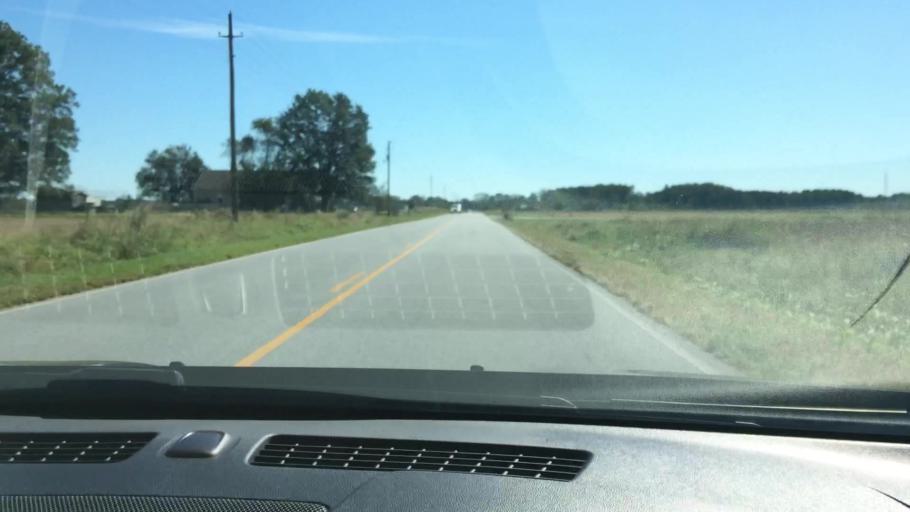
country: US
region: North Carolina
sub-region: Pitt County
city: Grifton
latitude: 35.3839
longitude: -77.3766
